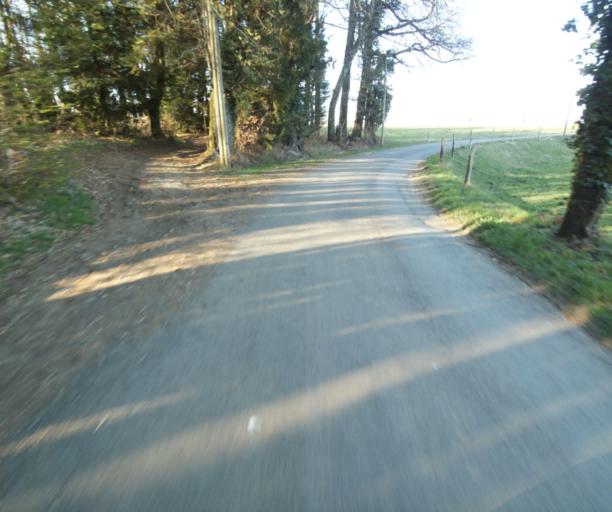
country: FR
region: Limousin
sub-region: Departement de la Correze
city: Seilhac
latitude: 45.3589
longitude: 1.7001
